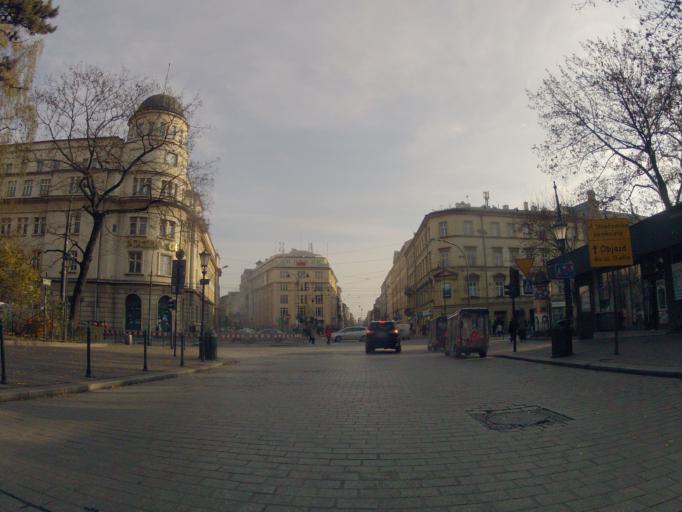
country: PL
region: Lesser Poland Voivodeship
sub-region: Krakow
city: Krakow
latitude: 50.0600
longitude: 19.9418
